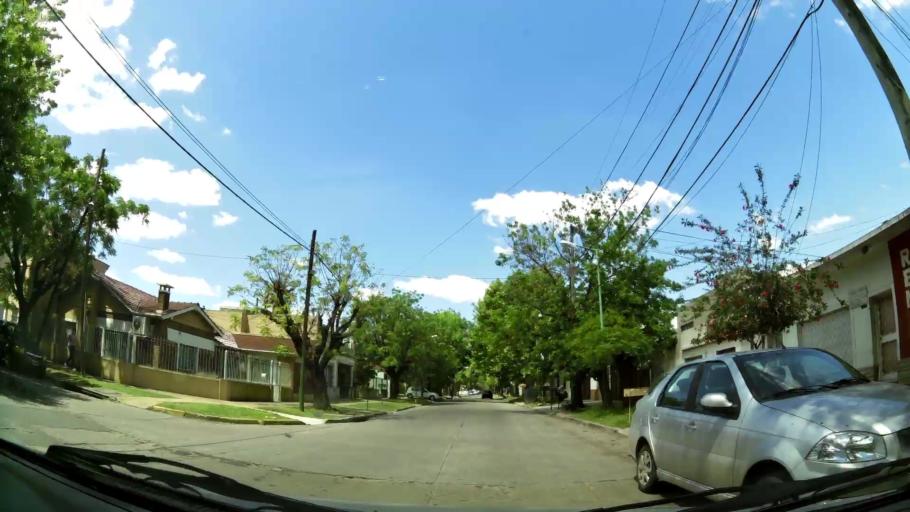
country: AR
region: Buenos Aires
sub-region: Partido de Lomas de Zamora
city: Lomas de Zamora
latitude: -34.7382
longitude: -58.4108
